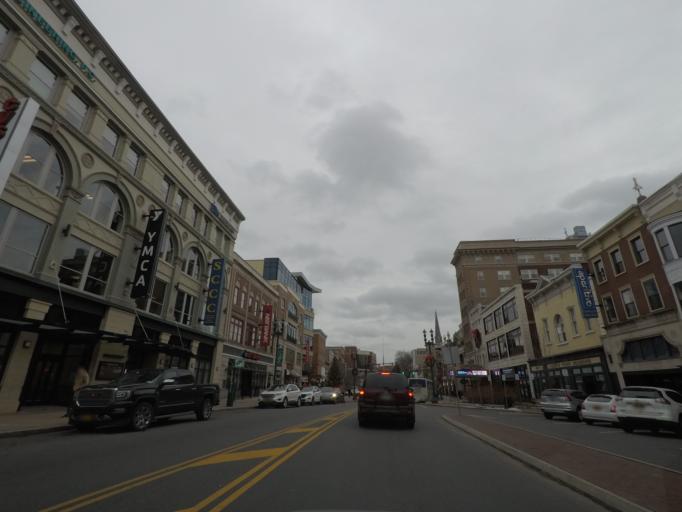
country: US
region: New York
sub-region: Schenectady County
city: Schenectady
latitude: 42.8131
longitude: -73.9422
